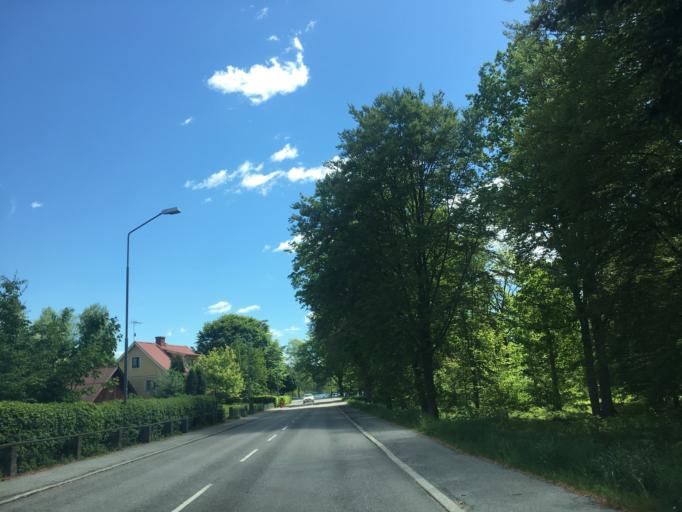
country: SE
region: Blekinge
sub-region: Olofstroms Kommun
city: Olofstroem
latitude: 56.3538
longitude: 14.5899
